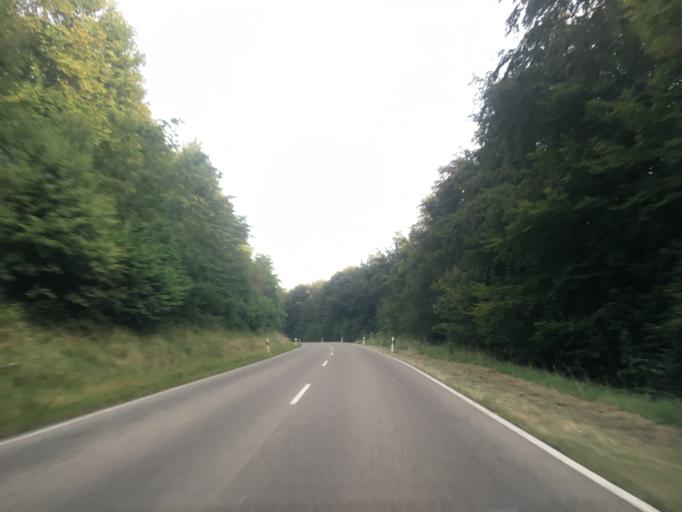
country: DE
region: Baden-Wuerttemberg
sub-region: Tuebingen Region
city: Sankt Johann
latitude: 48.4892
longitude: 9.3177
